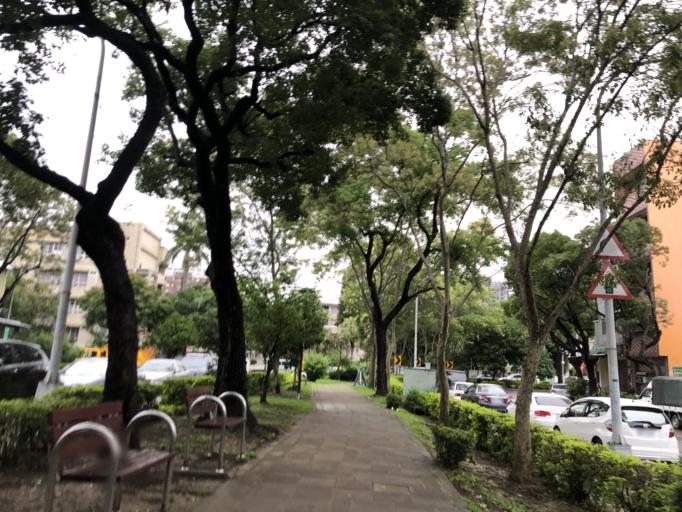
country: TW
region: Taiwan
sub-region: Taichung City
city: Taichung
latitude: 24.1534
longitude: 120.6732
